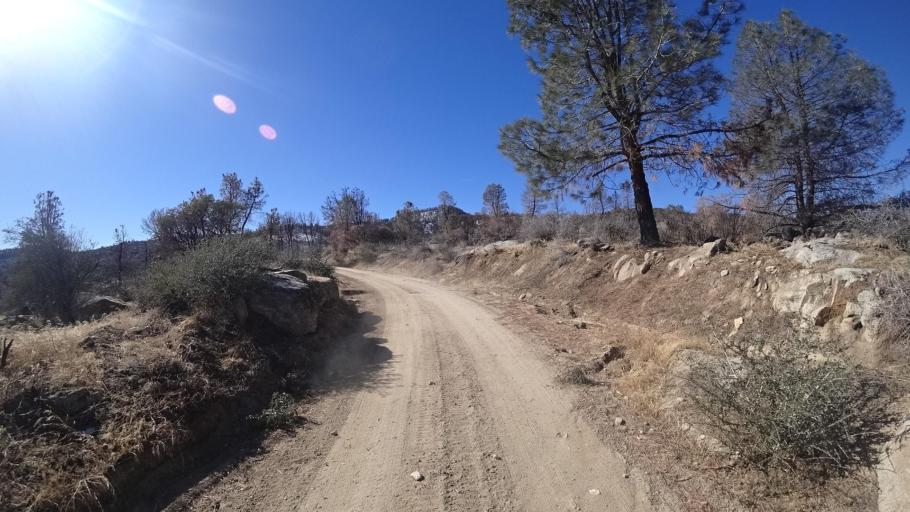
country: US
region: California
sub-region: Kern County
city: Alta Sierra
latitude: 35.7149
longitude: -118.5204
